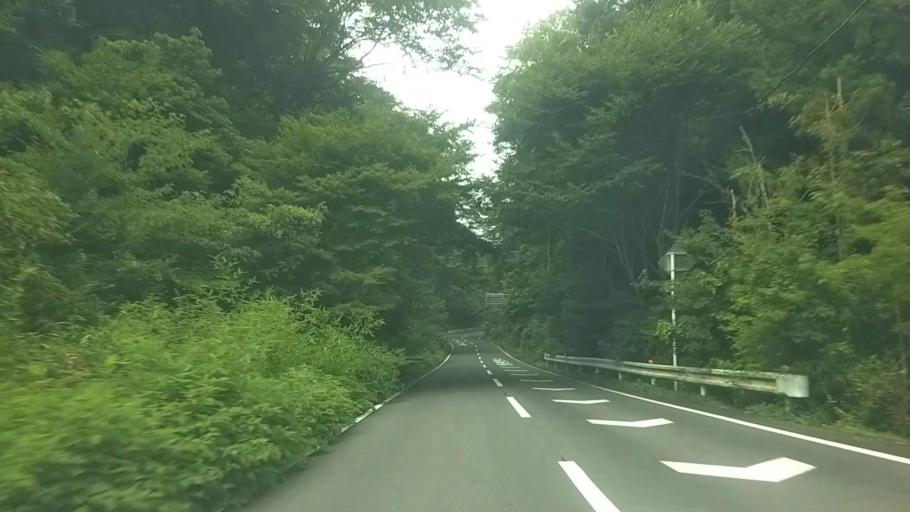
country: JP
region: Chiba
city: Kawaguchi
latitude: 35.2342
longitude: 140.0308
